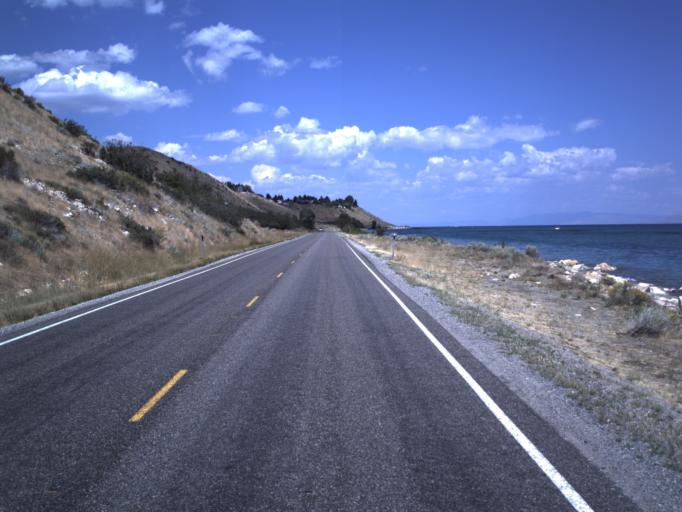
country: US
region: Utah
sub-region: Rich County
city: Randolph
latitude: 41.8785
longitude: -111.3655
